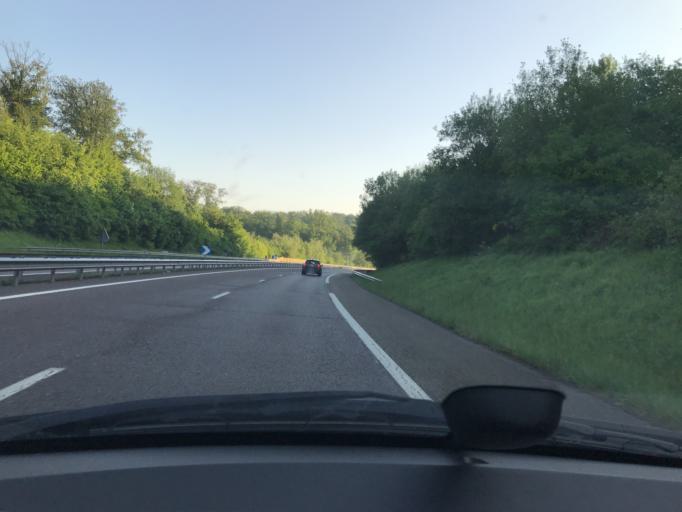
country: DE
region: Saarland
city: Kleinblittersdorf
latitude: 49.1271
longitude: 7.0345
